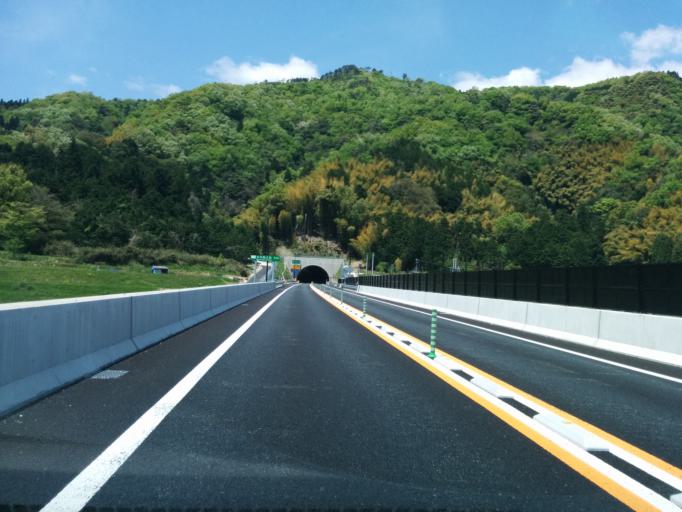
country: JP
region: Kyoto
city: Miyazu
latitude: 35.5523
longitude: 135.1353
